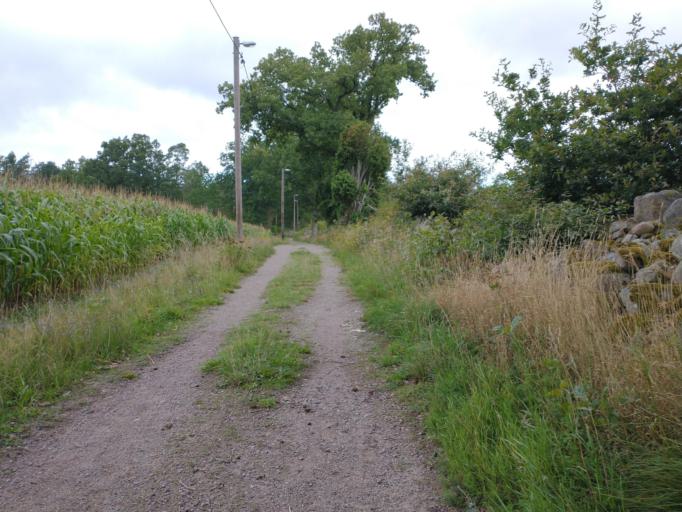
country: SE
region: Kalmar
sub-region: Kalmar Kommun
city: Lindsdal
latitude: 56.7757
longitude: 16.3003
